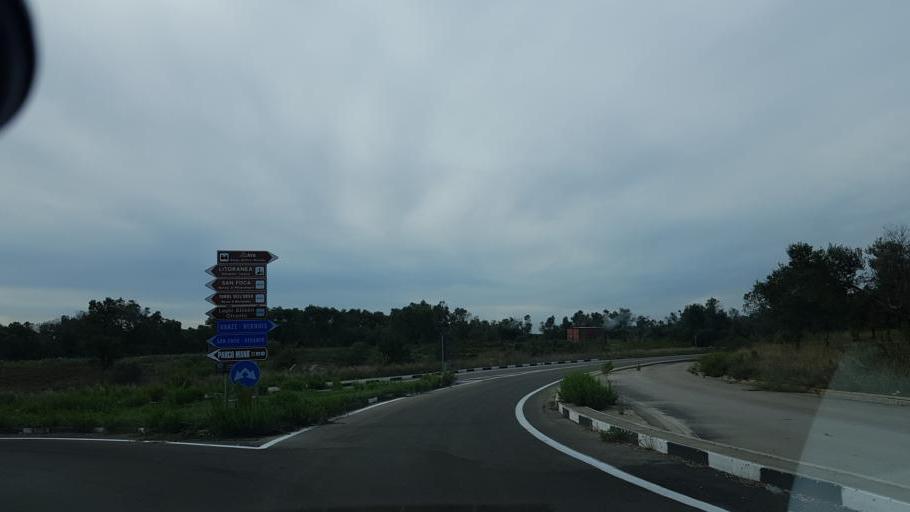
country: IT
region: Apulia
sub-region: Provincia di Lecce
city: Vernole
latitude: 40.3290
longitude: 18.3367
